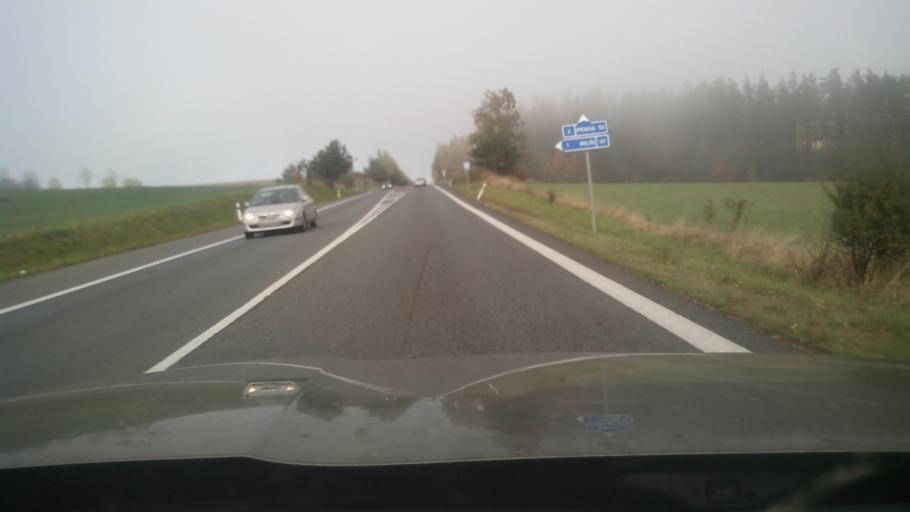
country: CZ
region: Central Bohemia
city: Milin
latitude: 49.6225
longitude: 14.0525
